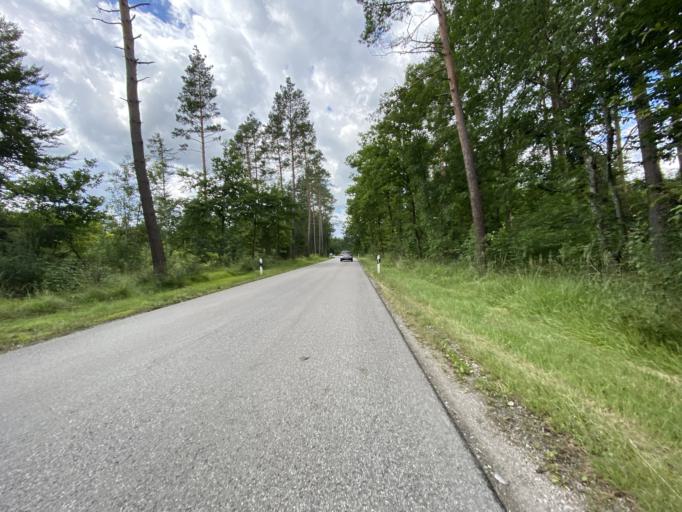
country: DE
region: Bavaria
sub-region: Upper Bavaria
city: Gauting
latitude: 48.0897
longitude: 11.3528
